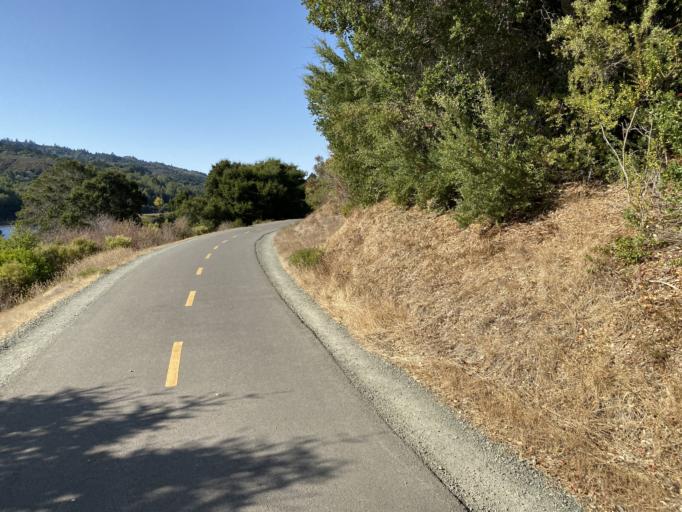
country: US
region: California
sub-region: San Mateo County
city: Hillsborough
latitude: 37.5524
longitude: -122.3862
